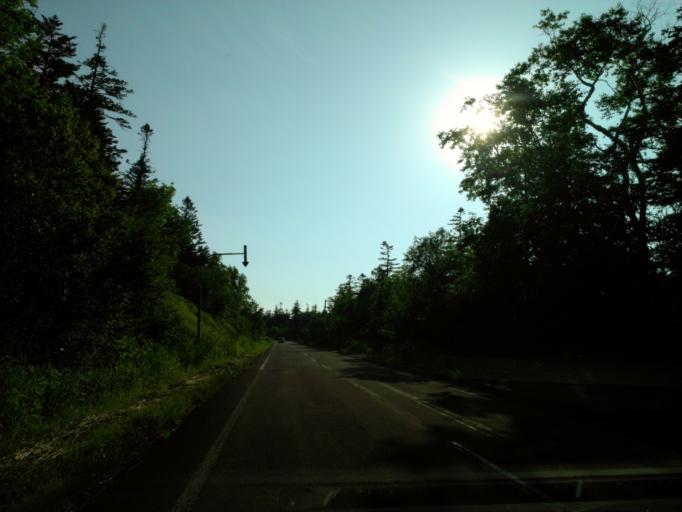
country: JP
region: Hokkaido
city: Shimo-furano
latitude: 43.4715
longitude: 142.6418
